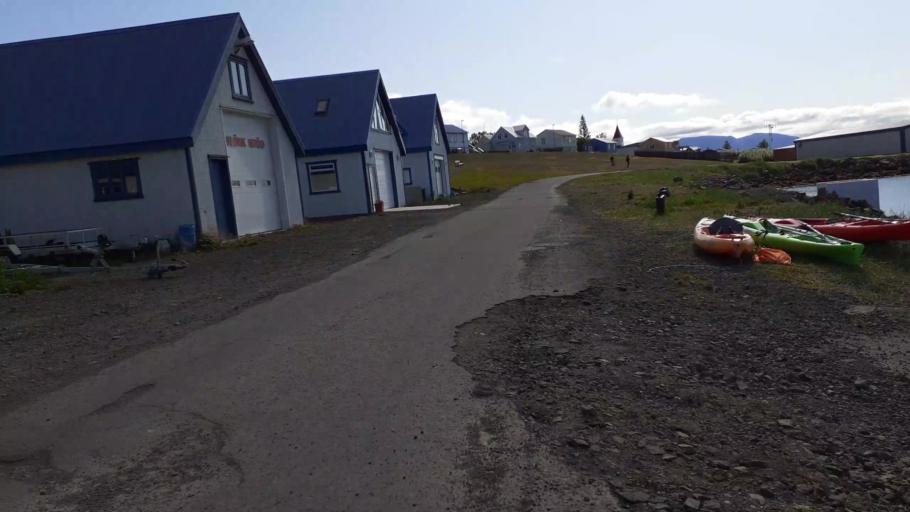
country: IS
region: Northeast
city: Dalvik
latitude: 65.9807
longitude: -18.3814
